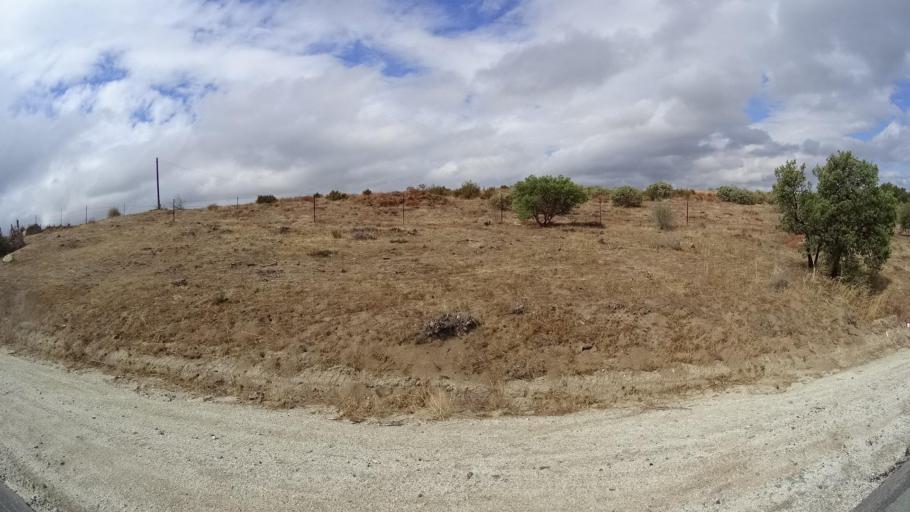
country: US
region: California
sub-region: San Diego County
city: Campo
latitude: 32.6581
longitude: -116.3152
